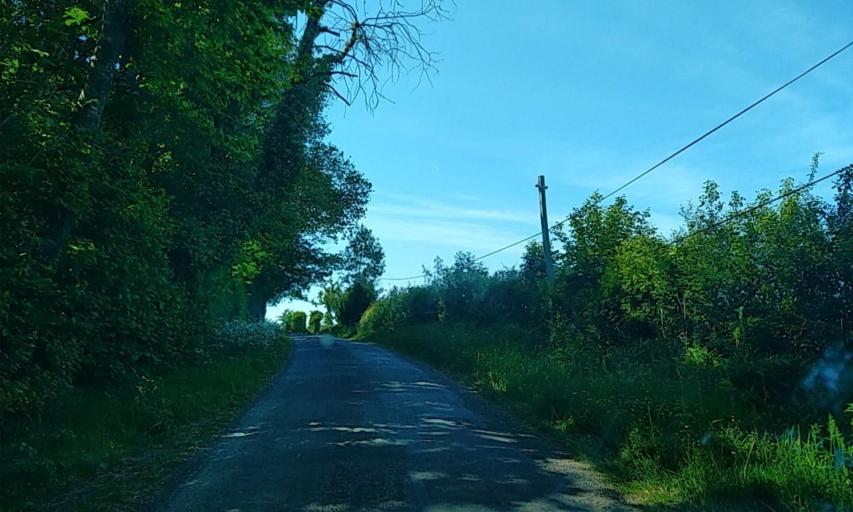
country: FR
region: Poitou-Charentes
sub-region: Departement des Deux-Sevres
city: Boisme
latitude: 46.7890
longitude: -0.4612
